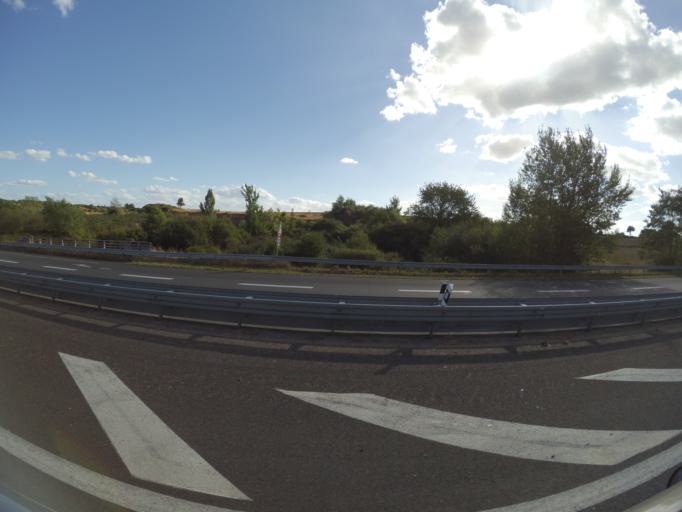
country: FR
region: Pays de la Loire
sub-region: Departement de Maine-et-Loire
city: Vihiers
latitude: 47.1402
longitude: -0.5598
